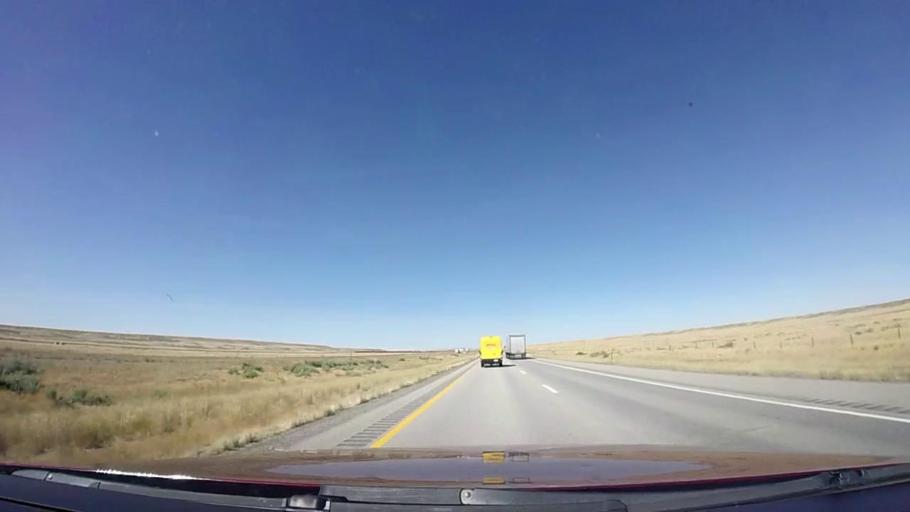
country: US
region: Wyoming
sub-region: Carbon County
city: Rawlins
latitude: 41.6602
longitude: -108.0707
